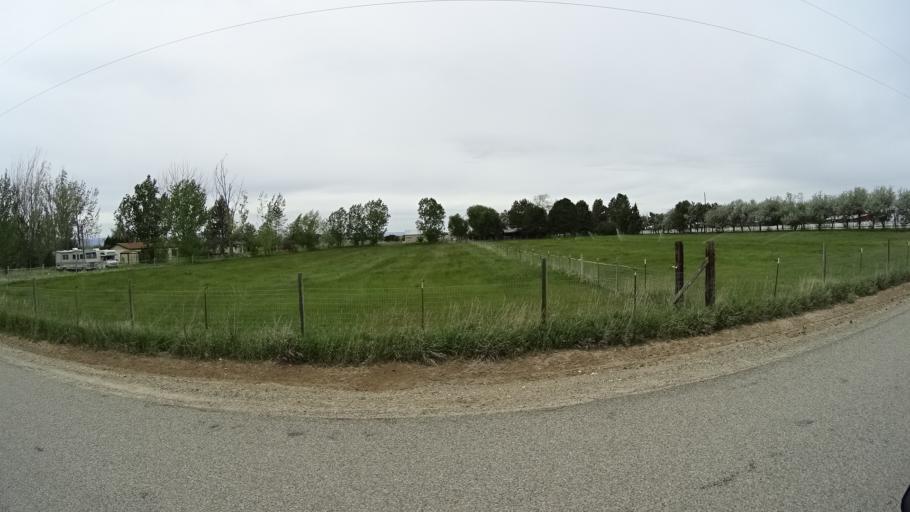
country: US
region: Idaho
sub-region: Ada County
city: Kuna
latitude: 43.4947
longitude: -116.3394
